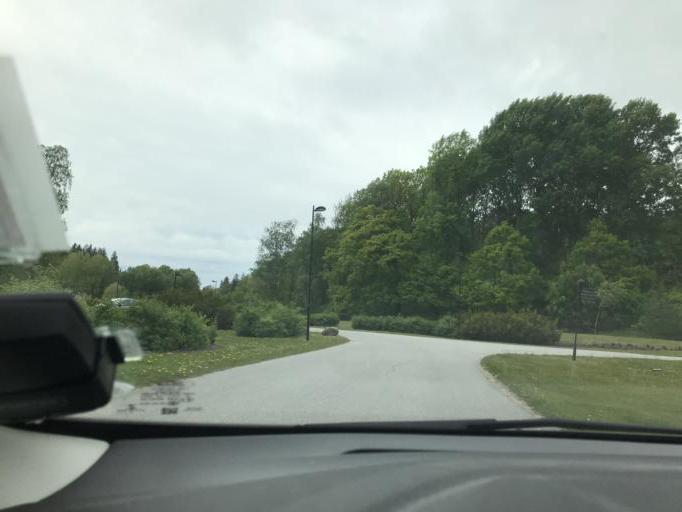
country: SE
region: Stockholm
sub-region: Botkyrka Kommun
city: Alby
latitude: 59.2182
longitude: 17.8502
